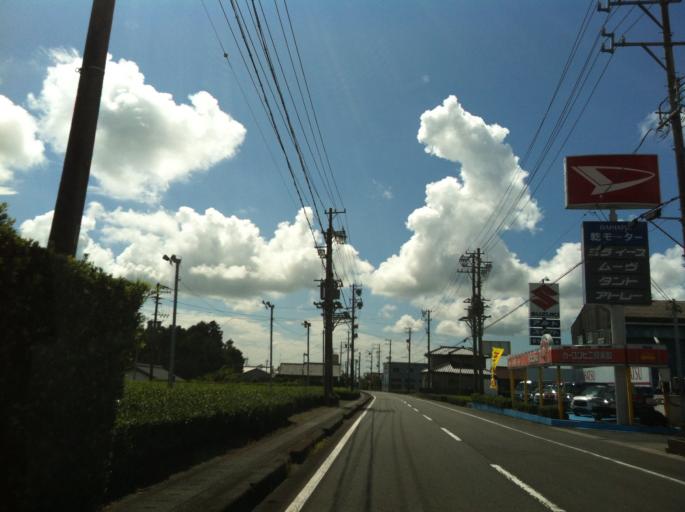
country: JP
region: Shizuoka
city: Kanaya
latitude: 34.7986
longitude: 138.1366
